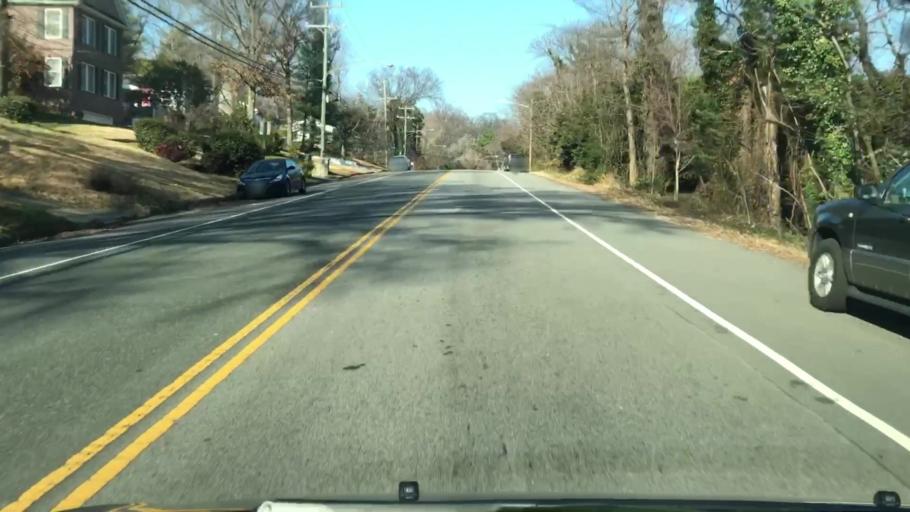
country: US
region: Virginia
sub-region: Fairfax County
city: Belle Haven
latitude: 38.7779
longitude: -77.0629
